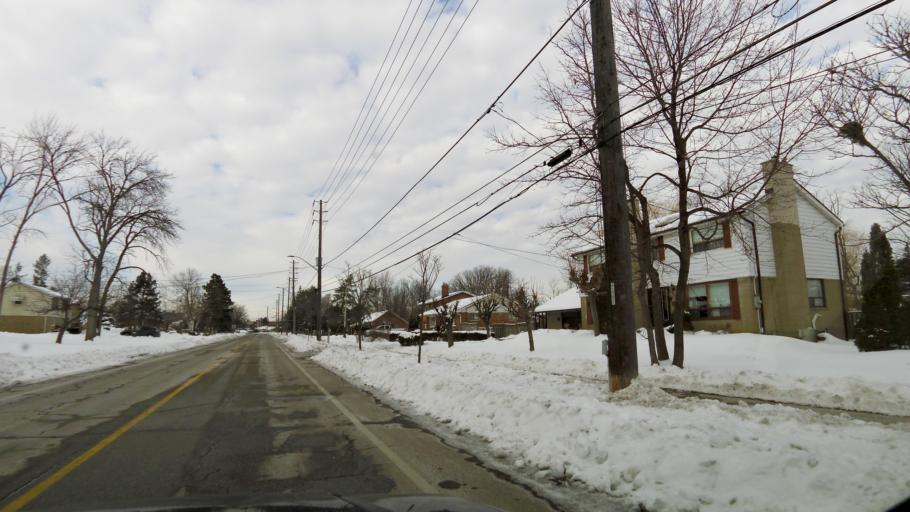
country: CA
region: Ontario
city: Mississauga
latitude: 43.5288
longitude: -79.6696
